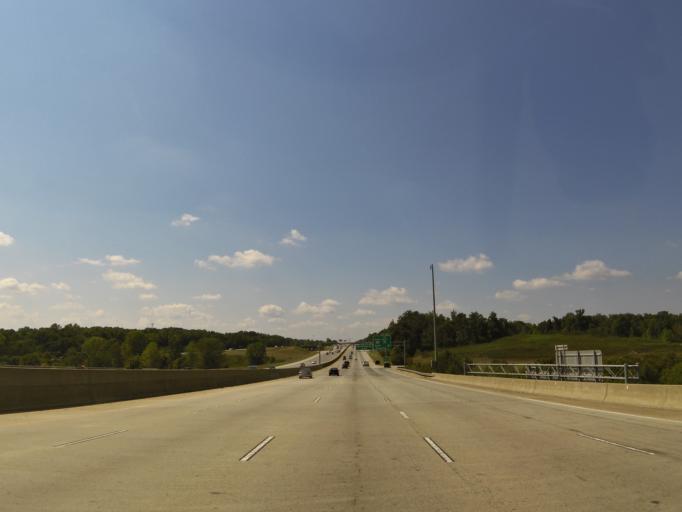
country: US
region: North Carolina
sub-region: Gaston County
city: Mount Holly
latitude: 35.2492
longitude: -80.9686
